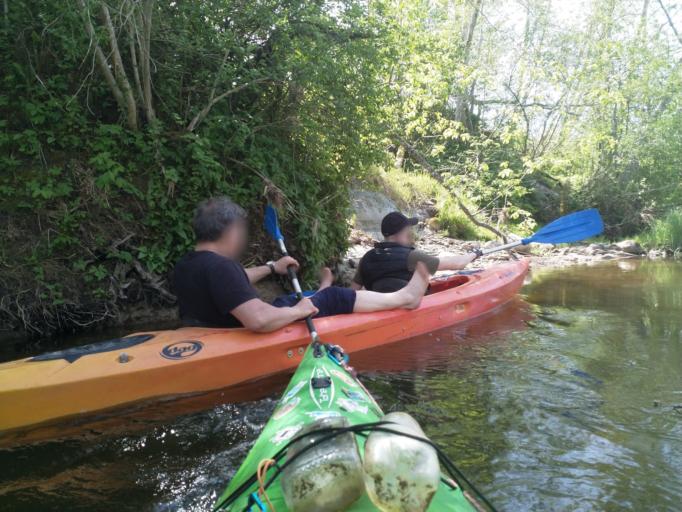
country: LV
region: Skrunda
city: Skrunda
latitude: 56.6983
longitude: 22.1841
